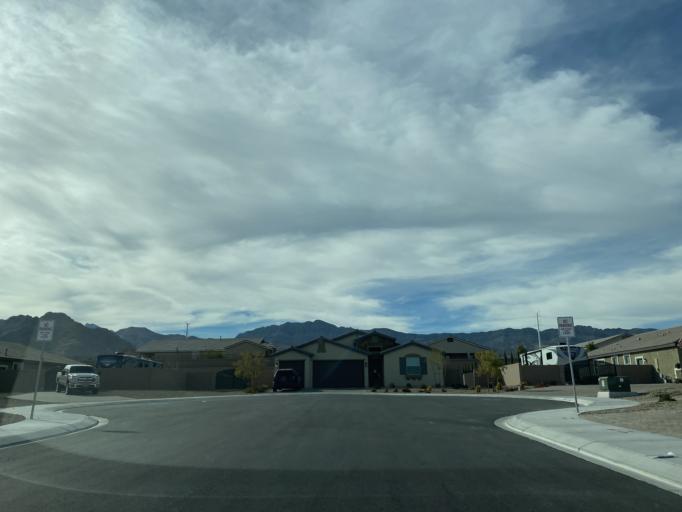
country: US
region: Nevada
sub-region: Clark County
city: Summerlin South
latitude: 36.2685
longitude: -115.3255
